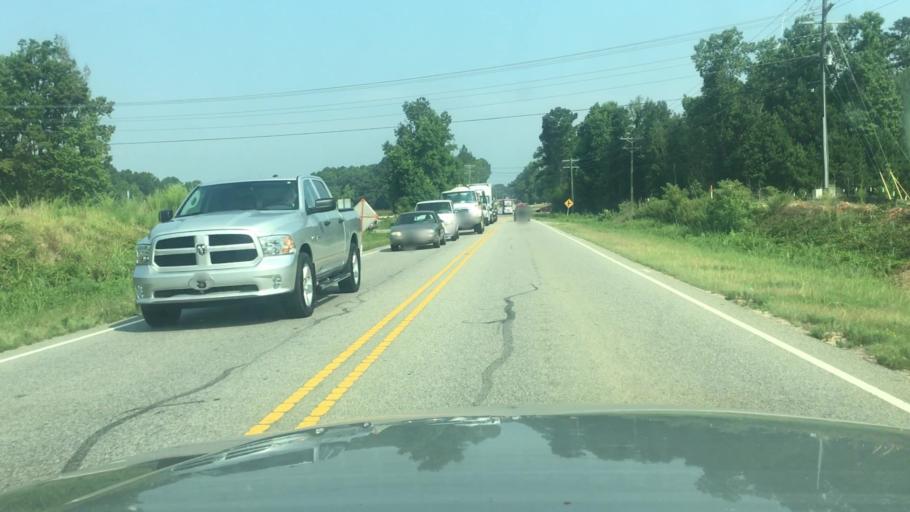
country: US
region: North Carolina
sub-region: Cumberland County
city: Hope Mills
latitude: 34.9281
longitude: -78.9124
